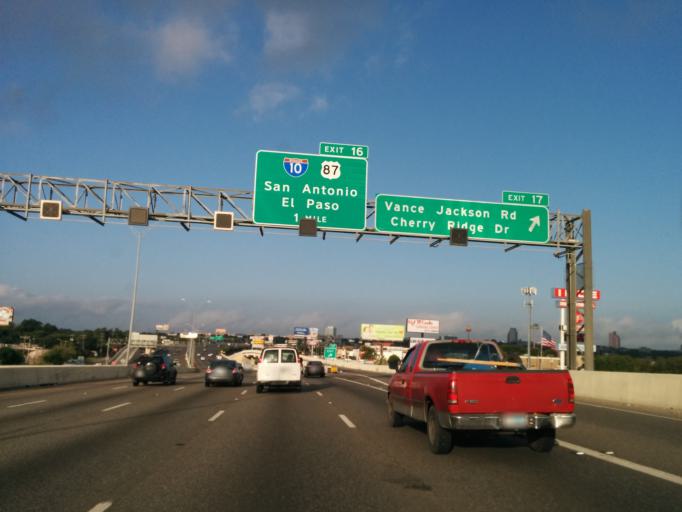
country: US
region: Texas
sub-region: Bexar County
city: Castle Hills
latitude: 29.5161
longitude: -98.5289
